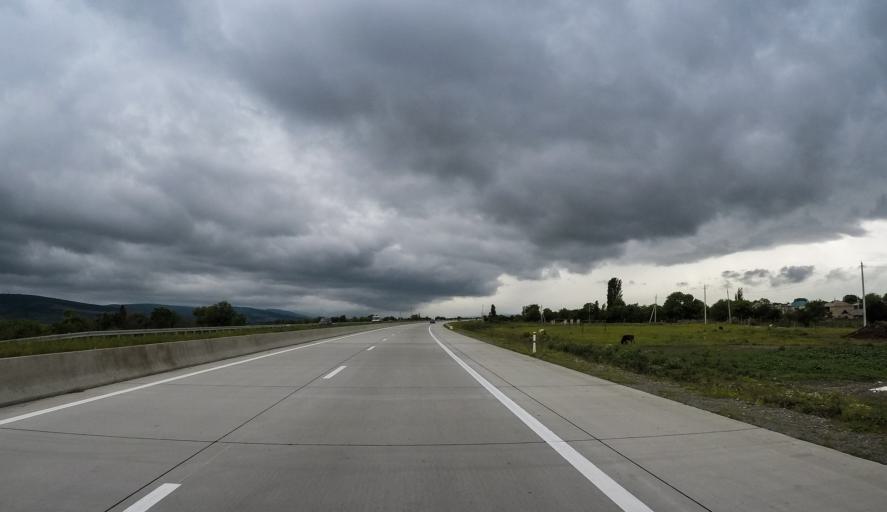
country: GE
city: Agara
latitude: 42.0292
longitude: 43.8345
